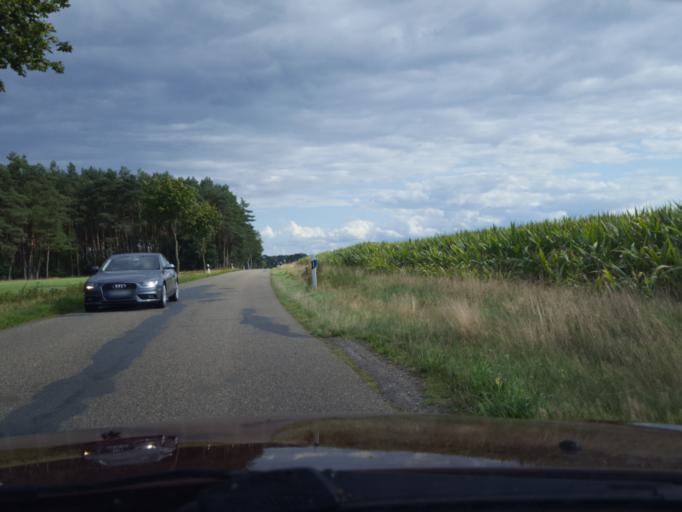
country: DE
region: Lower Saxony
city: Hemsbunde
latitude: 53.0779
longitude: 9.4609
